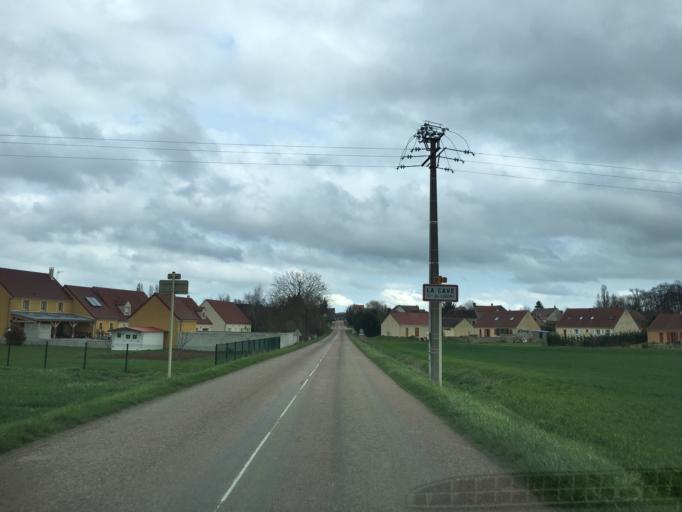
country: FR
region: Bourgogne
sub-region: Departement de l'Yonne
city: Charbuy
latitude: 47.8002
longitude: 3.4316
